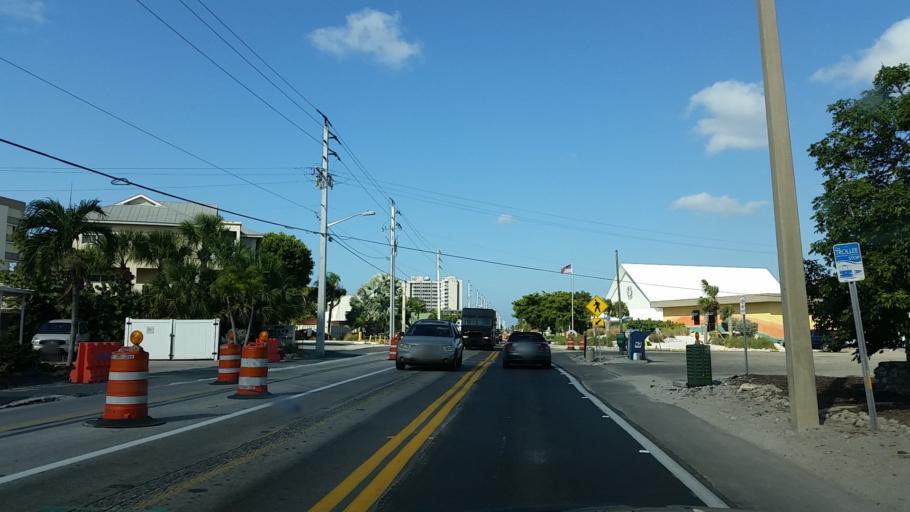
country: US
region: Florida
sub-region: Lee County
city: Fort Myers Beach
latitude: 26.4483
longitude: -81.9415
